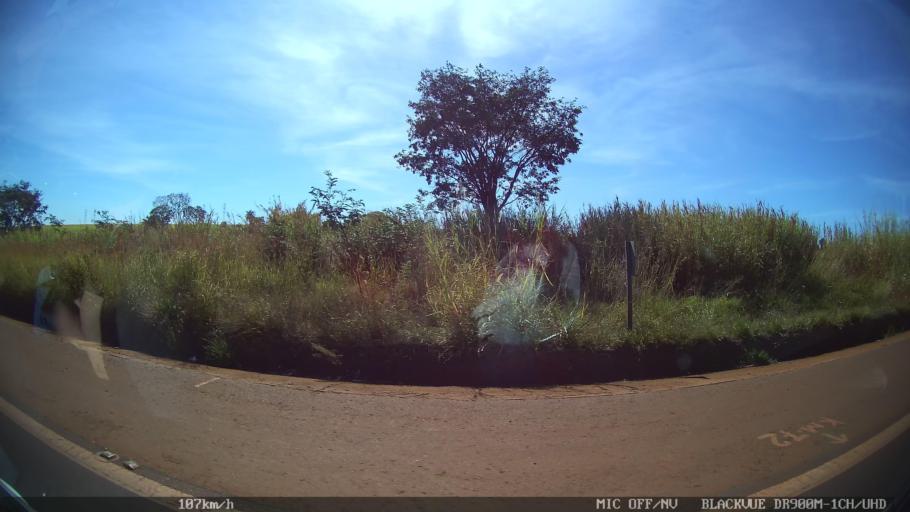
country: BR
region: Sao Paulo
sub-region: Sao Joaquim Da Barra
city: Sao Joaquim da Barra
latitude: -20.5515
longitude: -47.7385
